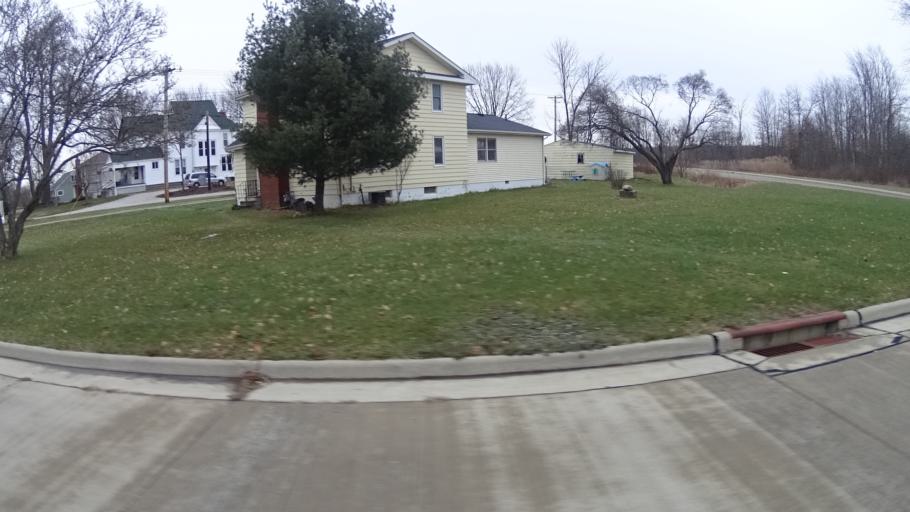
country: US
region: Ohio
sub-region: Lorain County
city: Grafton
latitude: 41.2766
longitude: -82.0512
